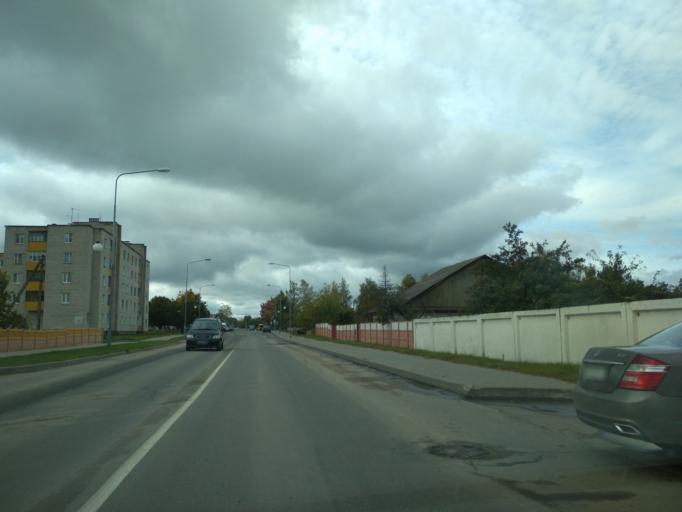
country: BY
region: Minsk
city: Mar''ina Horka
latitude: 53.5187
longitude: 28.1466
